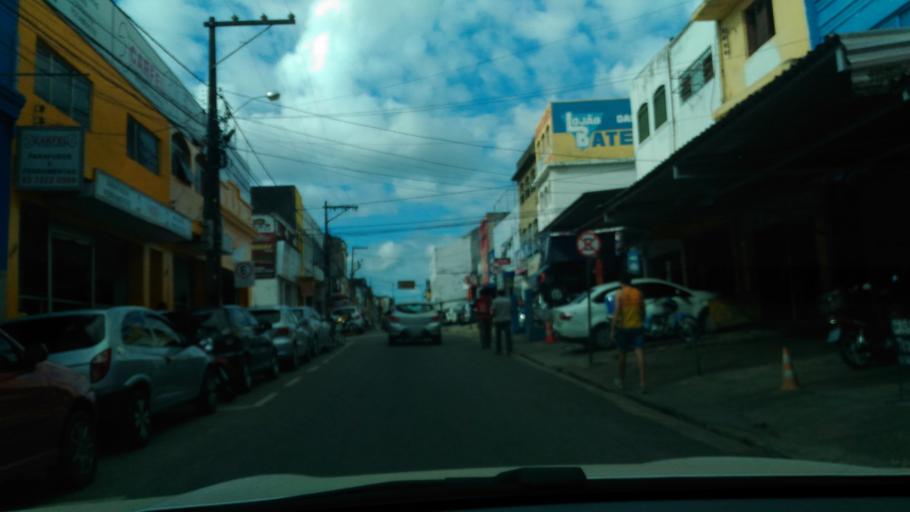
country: BR
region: Paraiba
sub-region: Joao Pessoa
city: Joao Pessoa
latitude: -7.1179
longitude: -34.8890
